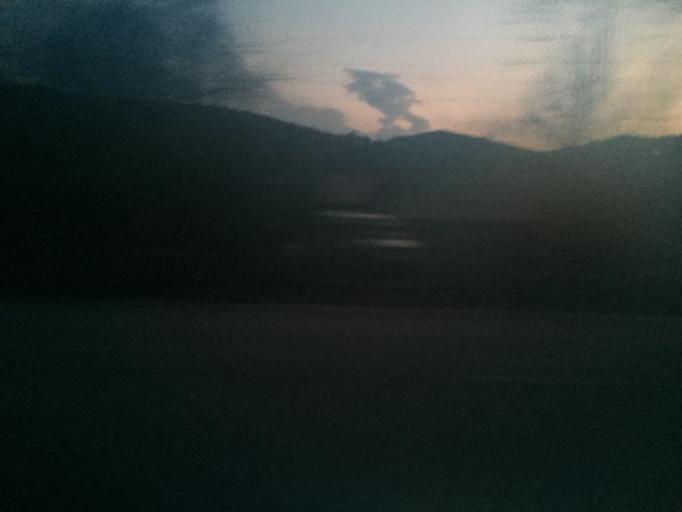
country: TR
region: Samsun
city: Kavak
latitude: 41.1343
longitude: 36.1284
